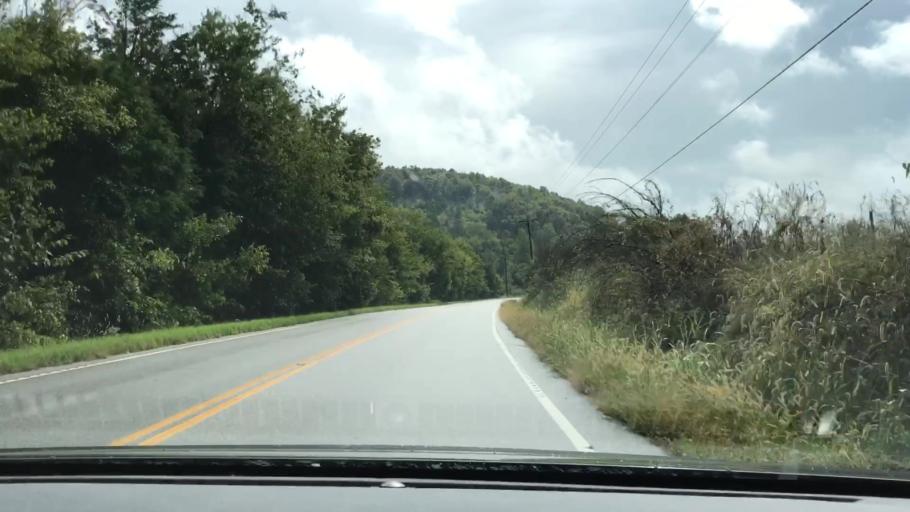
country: US
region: Tennessee
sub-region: Smith County
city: Carthage
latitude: 36.3408
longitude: -85.9652
